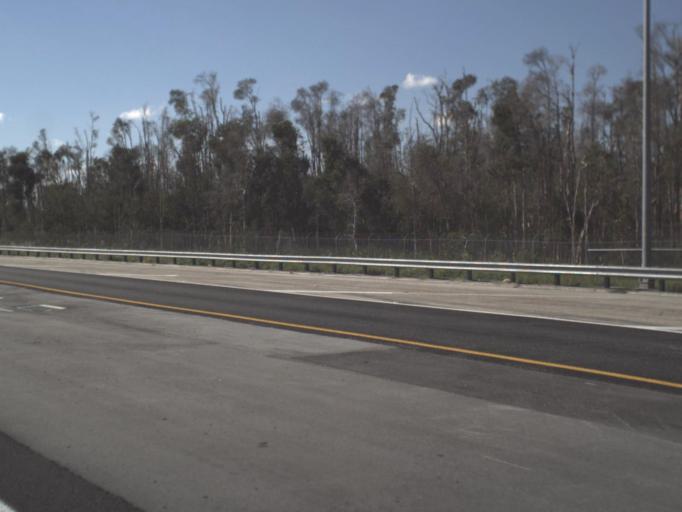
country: US
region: Florida
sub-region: Miami-Dade County
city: Doral
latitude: 25.8457
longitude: -80.3875
